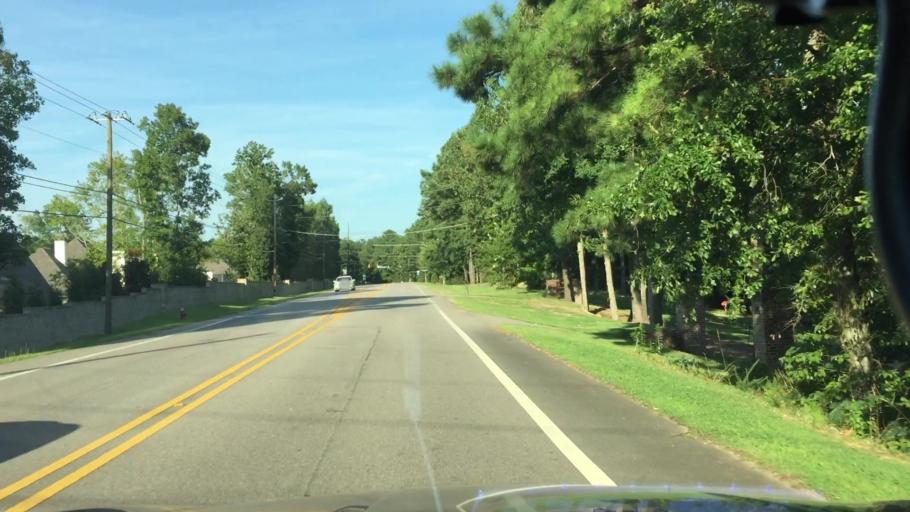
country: US
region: Alabama
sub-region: Lee County
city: Auburn
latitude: 32.5963
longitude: -85.4207
